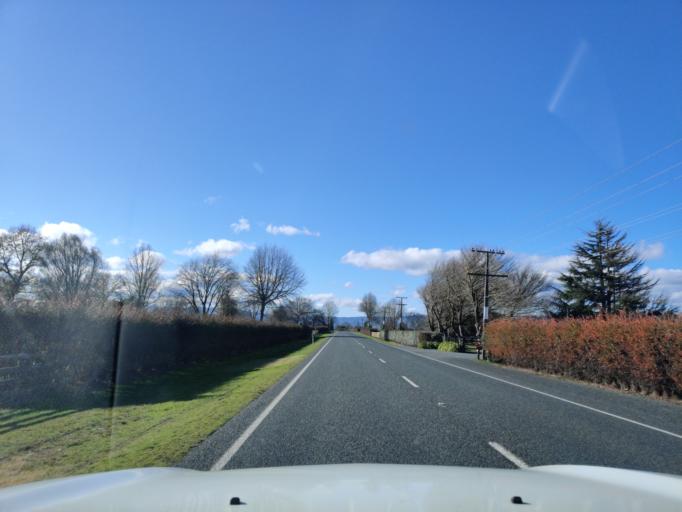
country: NZ
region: Waikato
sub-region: Matamata-Piako District
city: Matamata
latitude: -37.8682
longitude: 175.7490
